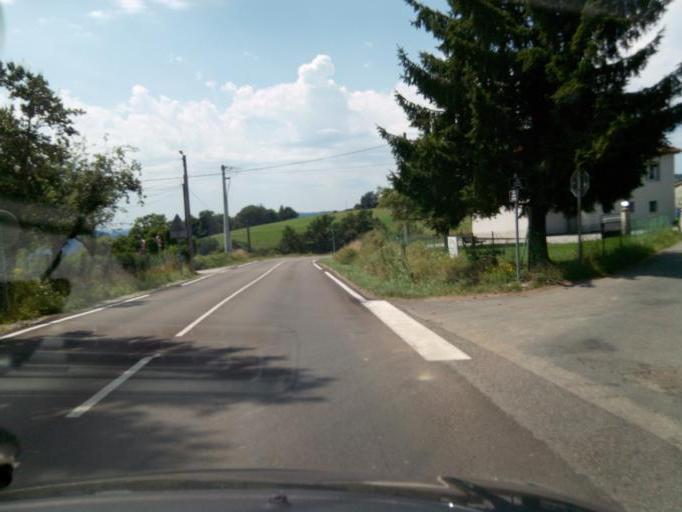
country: FR
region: Rhone-Alpes
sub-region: Departement de la Loire
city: La Ricamarie
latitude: 45.4145
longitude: 4.2951
